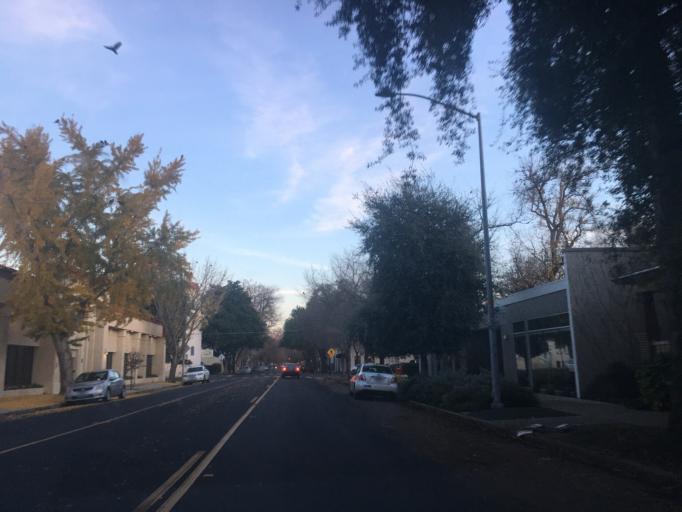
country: US
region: California
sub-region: Sacramento County
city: Sacramento
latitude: 38.5699
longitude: -121.4960
